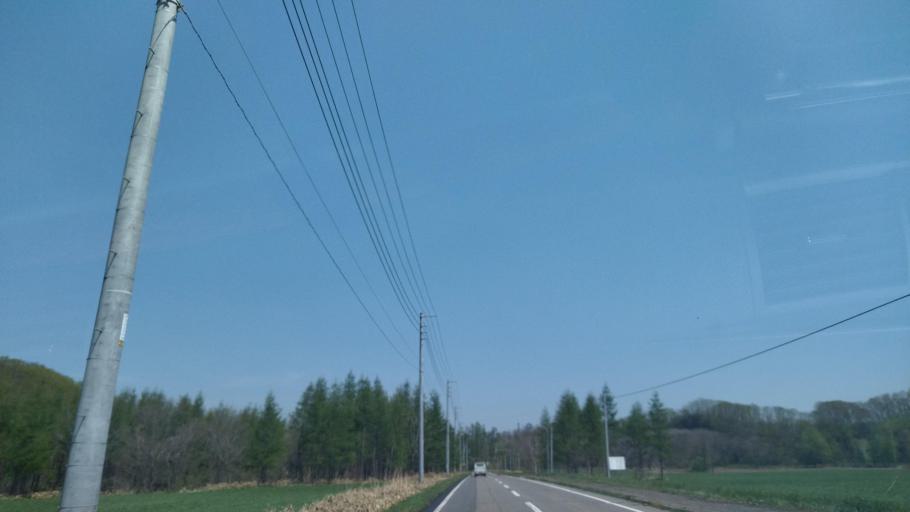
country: JP
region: Hokkaido
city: Obihiro
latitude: 42.8226
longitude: 142.9863
